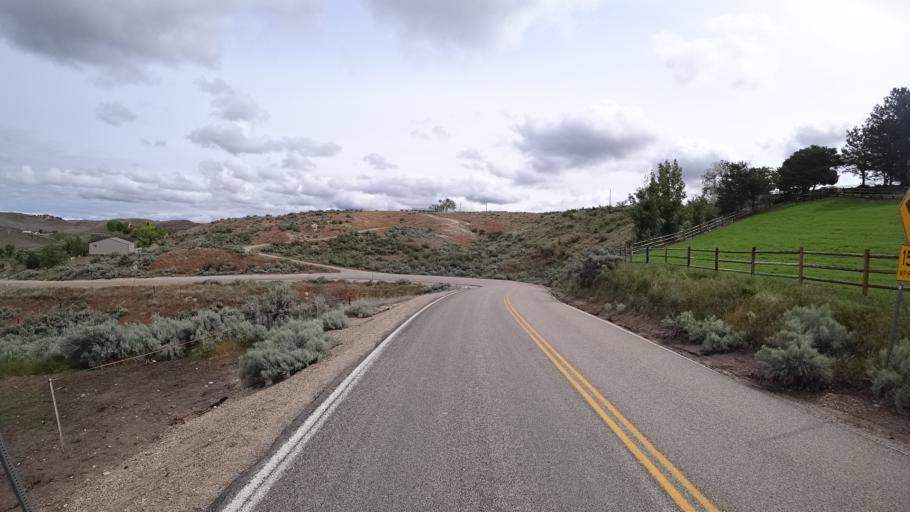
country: US
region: Idaho
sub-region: Ada County
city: Eagle
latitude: 43.7410
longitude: -116.3558
